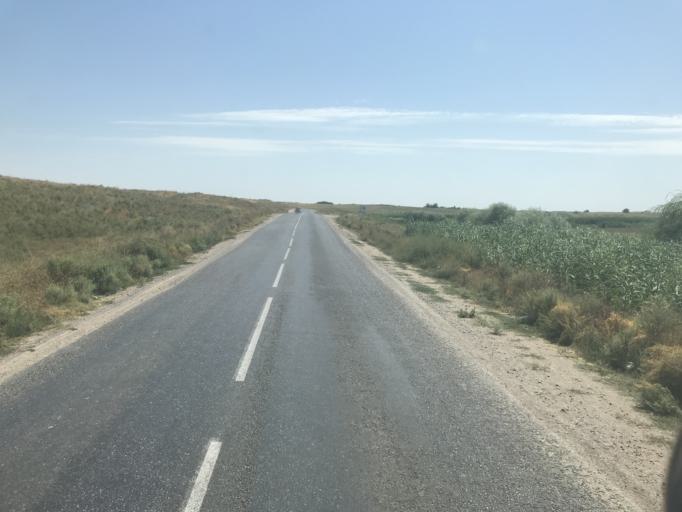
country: UZ
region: Toshkent
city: Yangiyul
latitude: 41.3534
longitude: 68.8638
